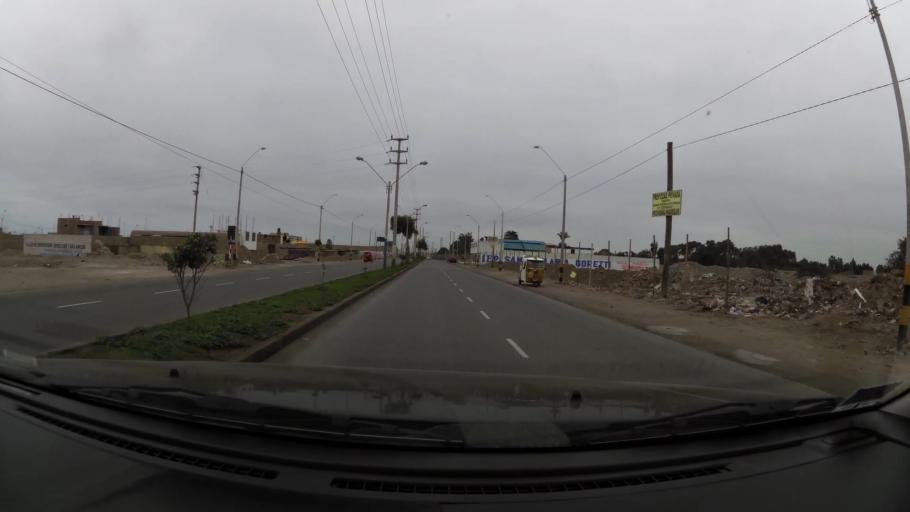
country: PE
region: Ica
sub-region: Provincia de Pisco
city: Pisco
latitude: -13.7157
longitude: -76.1946
